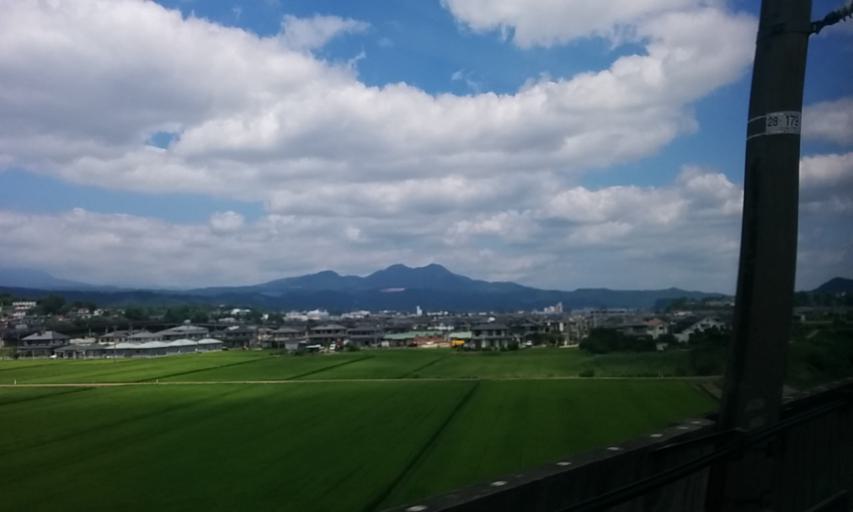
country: JP
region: Miyagi
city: Shiroishi
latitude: 37.9869
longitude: 140.6260
